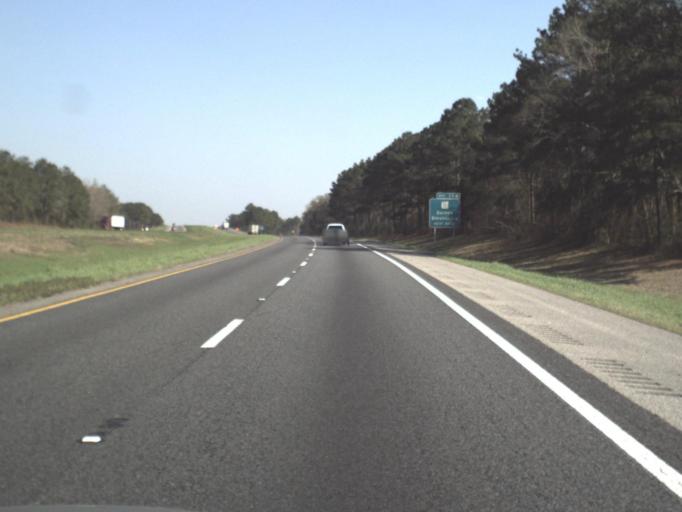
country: US
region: Florida
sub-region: Gadsden County
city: Gretna
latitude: 30.5808
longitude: -84.7081
